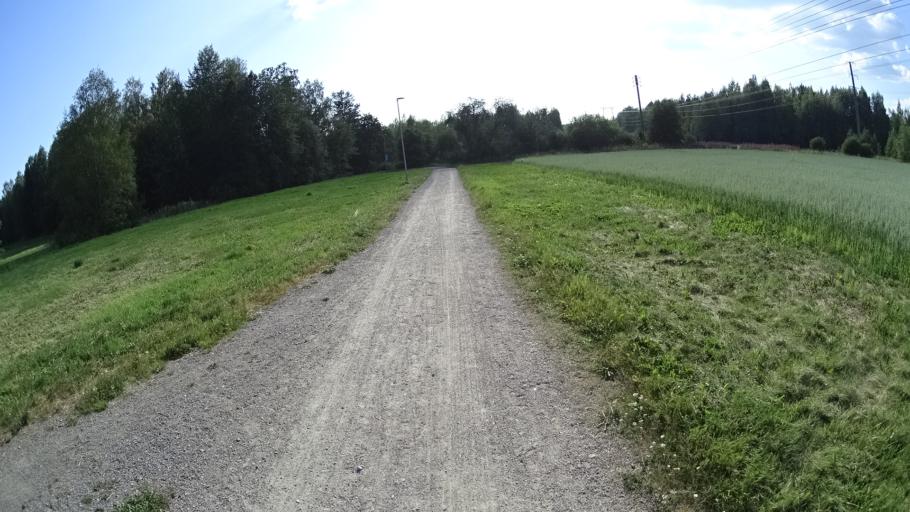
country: FI
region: Uusimaa
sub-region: Porvoo
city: Porvoo
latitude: 60.4041
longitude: 25.6462
